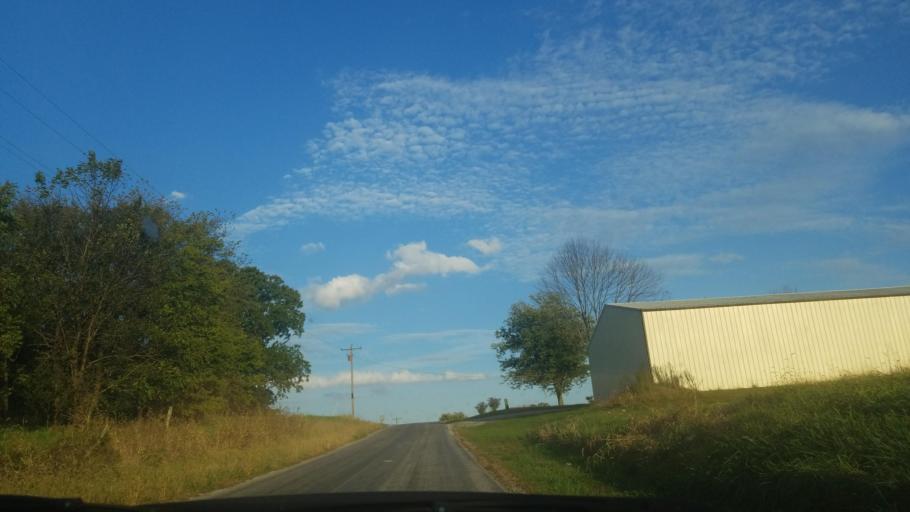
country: US
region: Illinois
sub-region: Saline County
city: Carrier Mills
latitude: 37.8050
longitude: -88.6565
